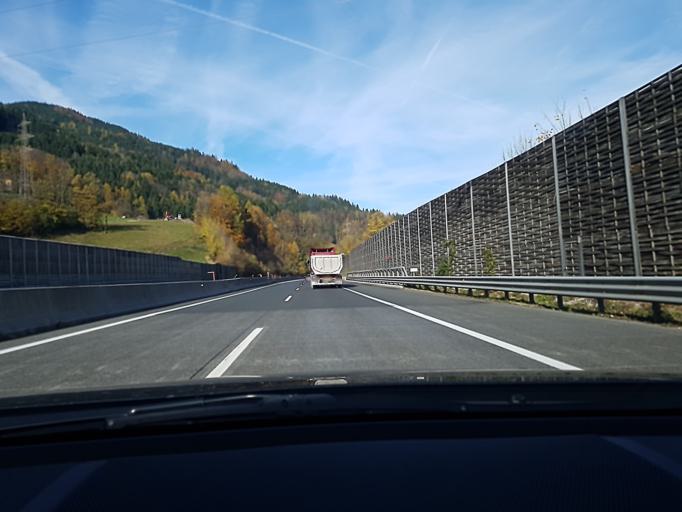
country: AT
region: Salzburg
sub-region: Politischer Bezirk Hallein
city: Kuchl
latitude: 47.6116
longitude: 13.1424
